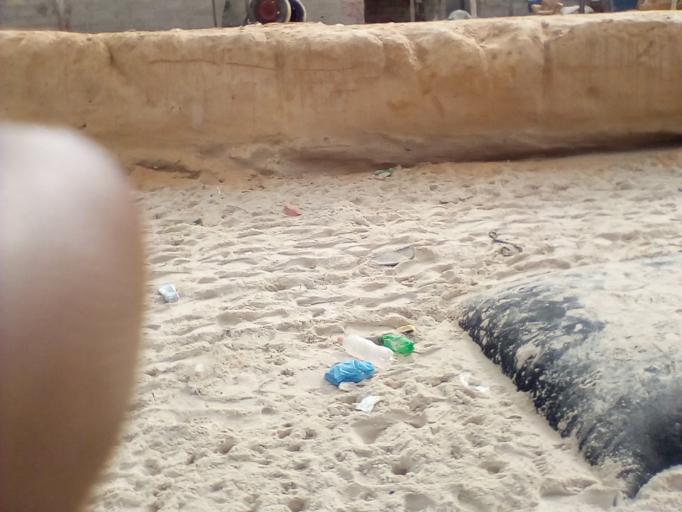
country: SN
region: Saint-Louis
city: Saint-Louis
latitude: 16.0432
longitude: -16.5088
